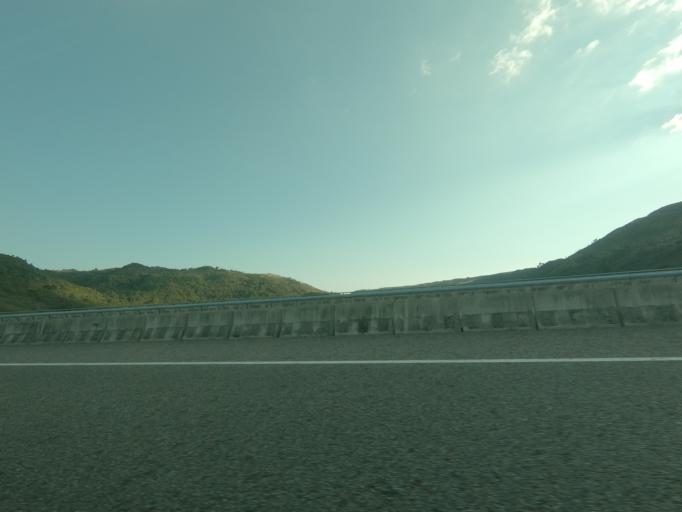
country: ES
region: Galicia
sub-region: Provincia de Ourense
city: Oimbra
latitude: 41.9278
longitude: -7.4994
